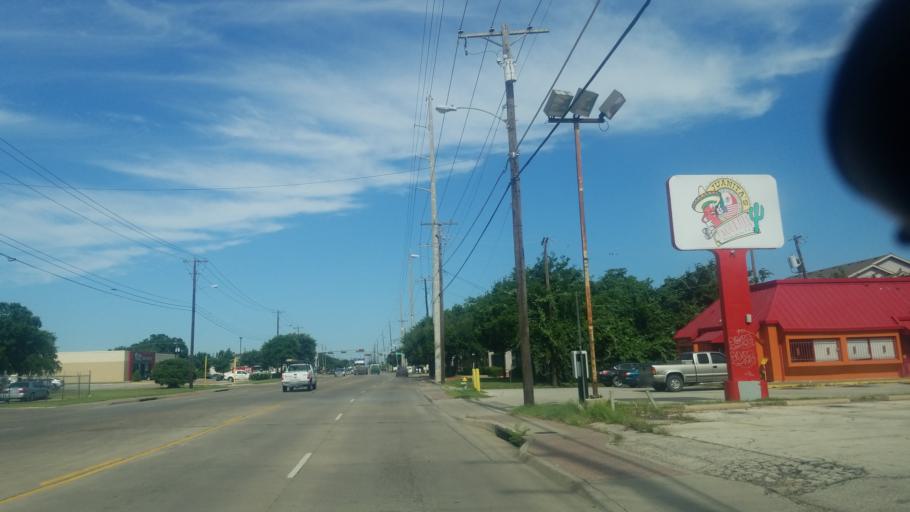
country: US
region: Texas
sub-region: Dallas County
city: Dallas
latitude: 32.7787
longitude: -96.8543
